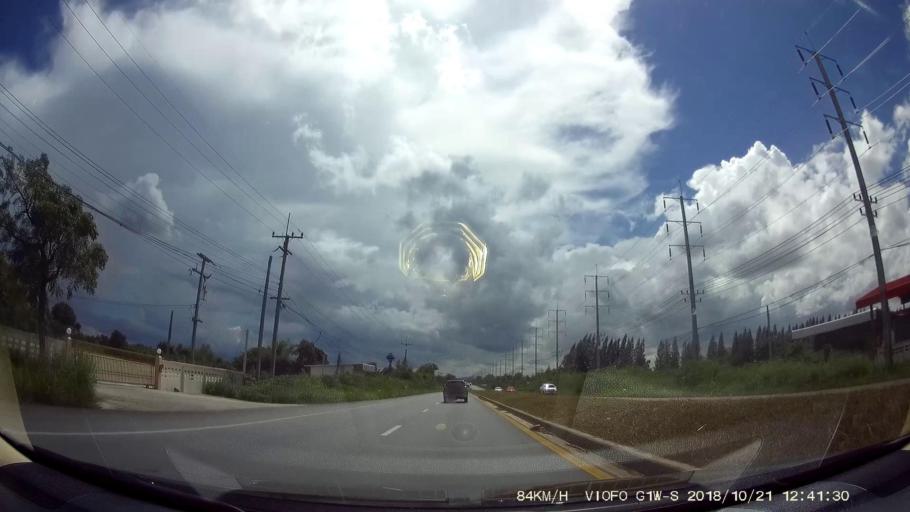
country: TH
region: Nakhon Ratchasima
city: Amphoe Sikhiu
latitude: 15.0119
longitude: 101.6868
